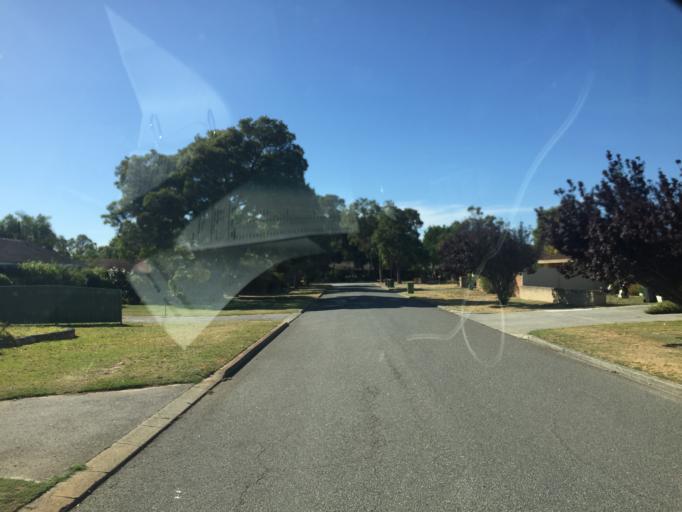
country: AU
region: Western Australia
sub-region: Gosnells
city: Maddington
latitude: -32.0578
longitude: 116.0014
